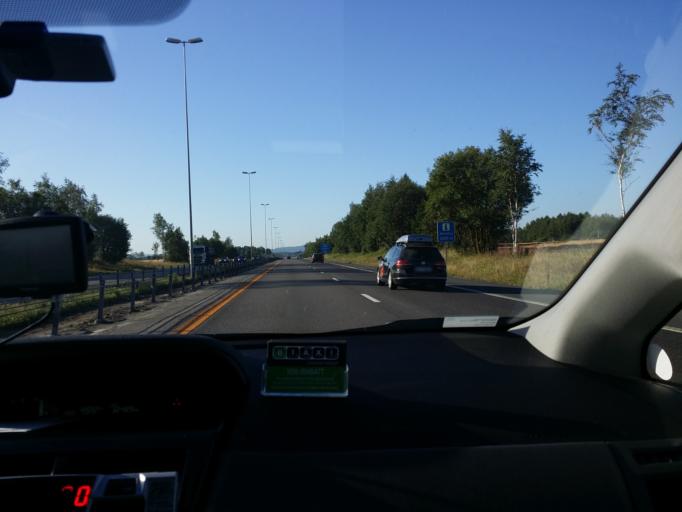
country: NO
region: Akershus
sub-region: Ullensaker
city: Klofta
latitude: 60.0957
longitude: 11.1443
